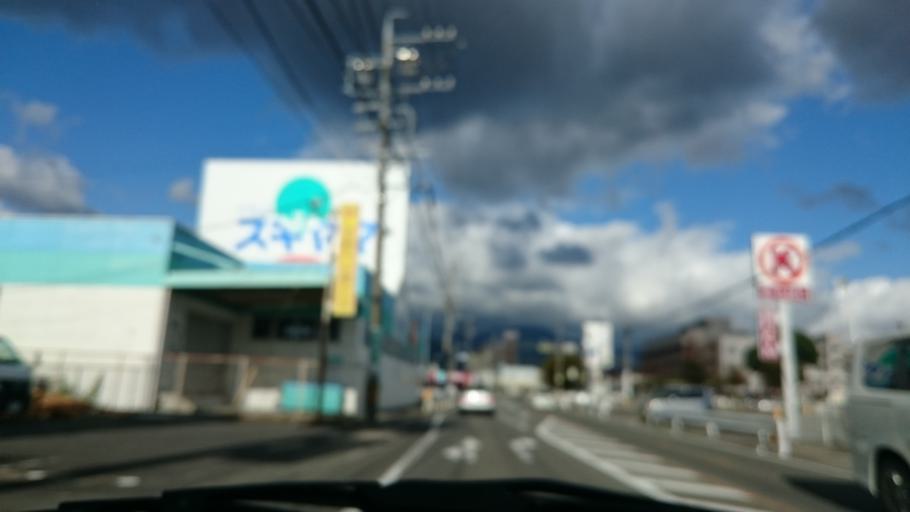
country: JP
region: Mie
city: Komono
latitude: 35.0070
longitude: 136.5221
